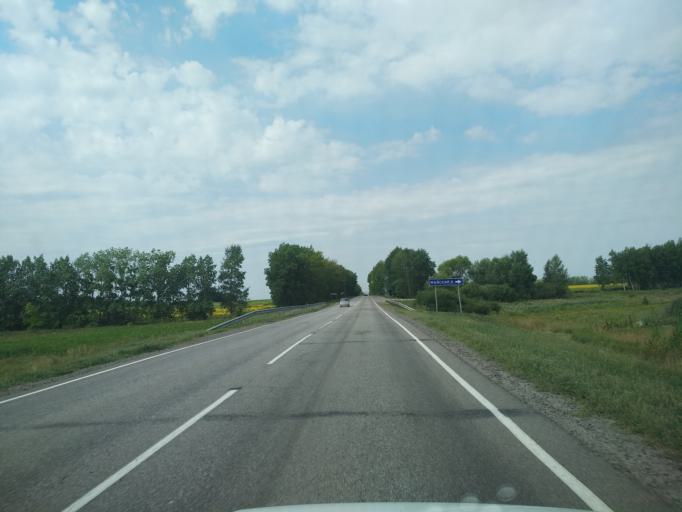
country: RU
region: Voronezj
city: Pereleshino
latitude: 51.7122
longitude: 40.0034
